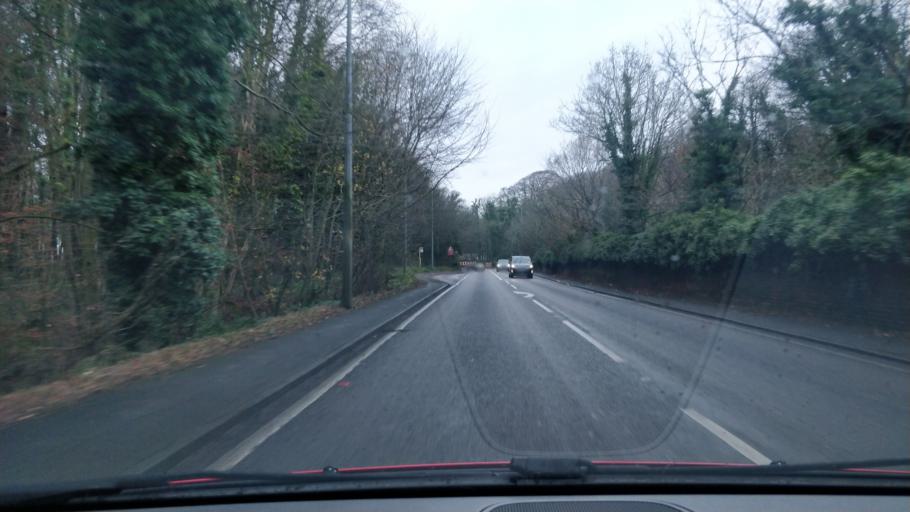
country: GB
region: England
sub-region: Sefton
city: Ince Blundell
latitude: 53.5149
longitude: -3.0169
